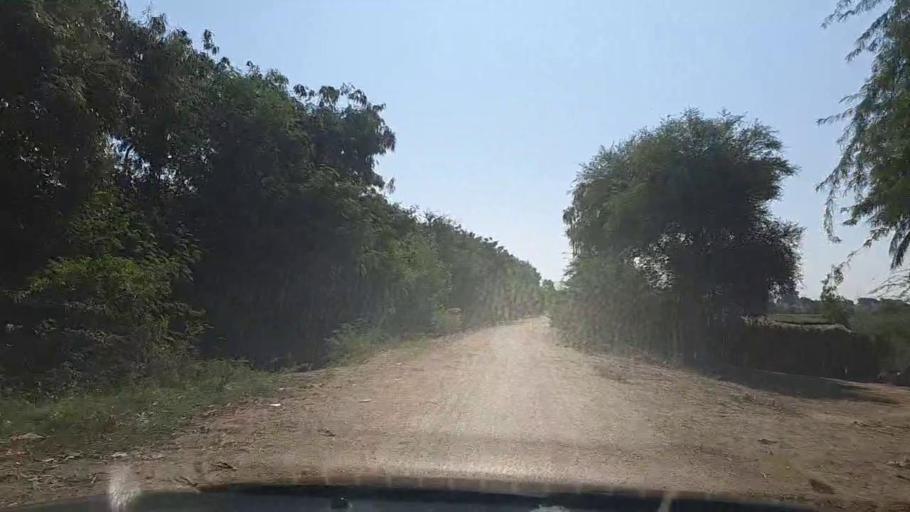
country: PK
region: Sindh
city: Thatta
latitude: 24.5932
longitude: 67.8196
